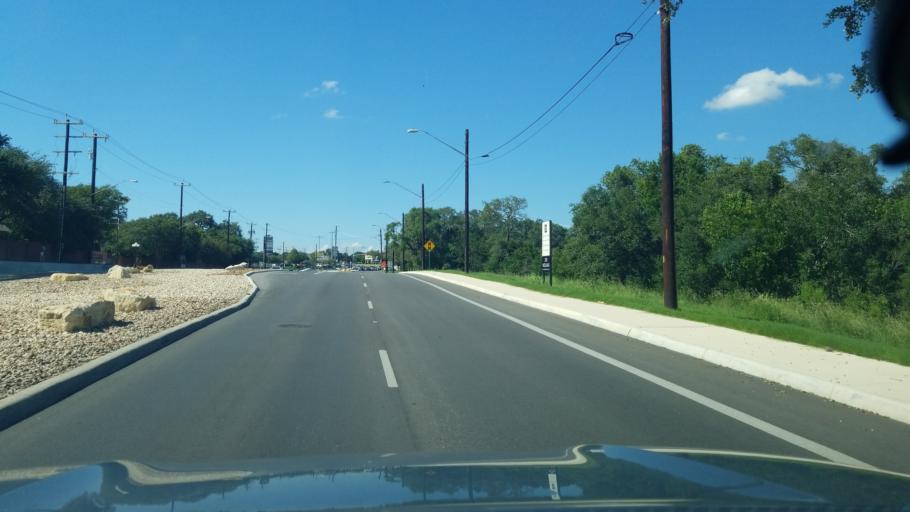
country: US
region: Texas
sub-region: Bexar County
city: Hollywood Park
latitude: 29.5996
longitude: -98.4414
